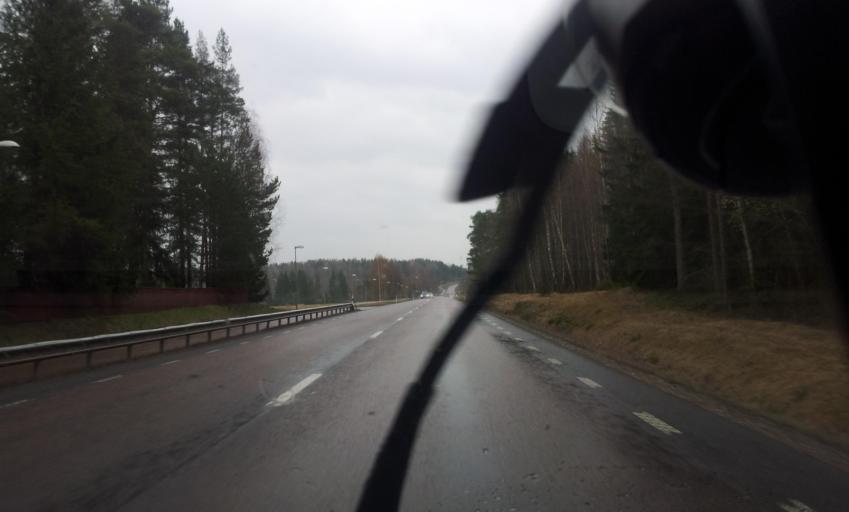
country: SE
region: Dalarna
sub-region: Borlange Kommun
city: Borlaenge
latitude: 60.5183
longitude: 15.3681
